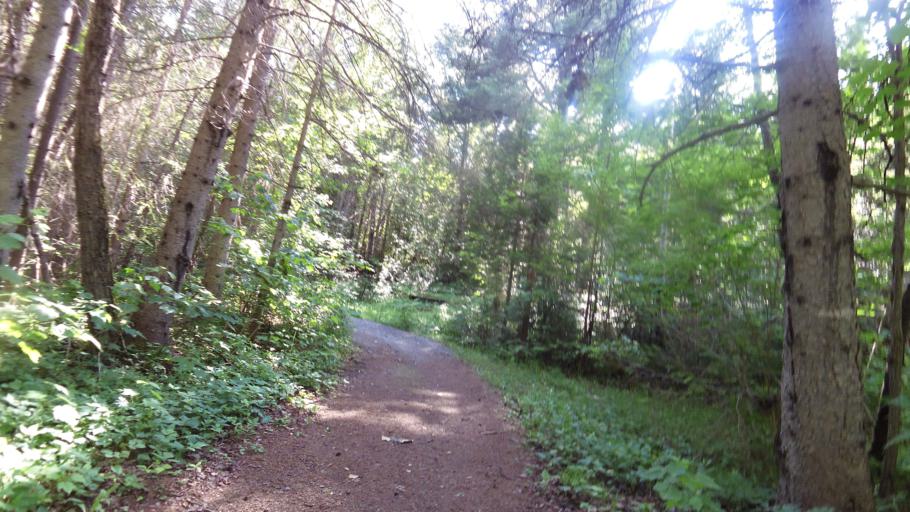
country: CA
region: Ontario
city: Temiskaming Shores
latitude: 47.3854
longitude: -79.6877
